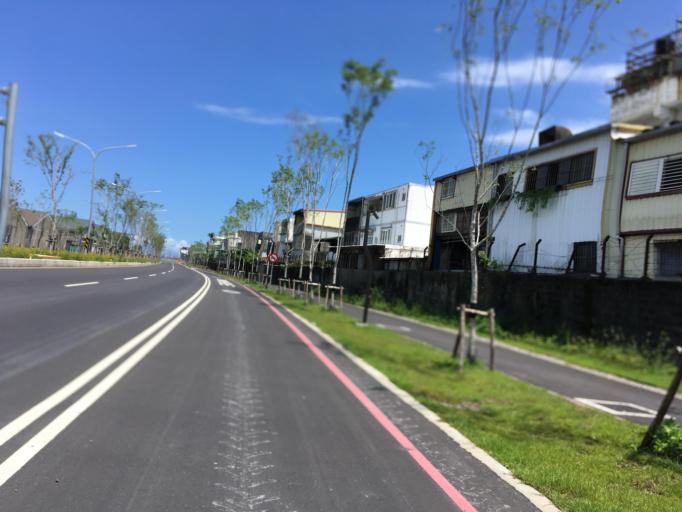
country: TW
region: Taiwan
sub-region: Yilan
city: Yilan
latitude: 24.6933
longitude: 121.7709
